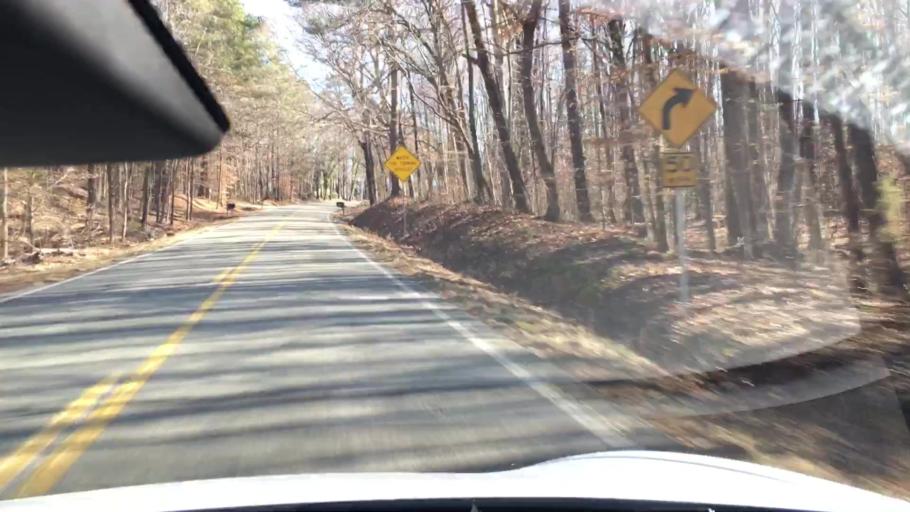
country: US
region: Virginia
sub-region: Henrico County
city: Short Pump
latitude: 37.5786
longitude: -77.7286
